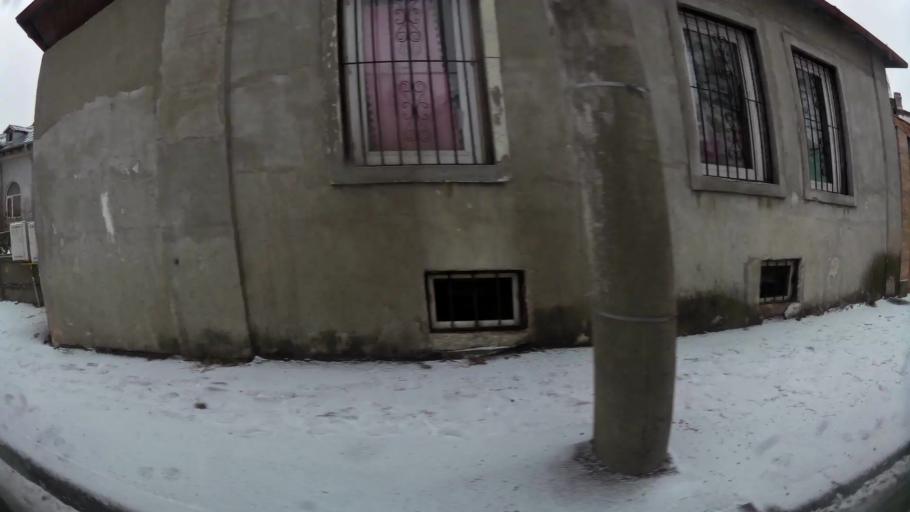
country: RO
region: Prahova
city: Ploiesti
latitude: 44.9467
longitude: 26.0308
